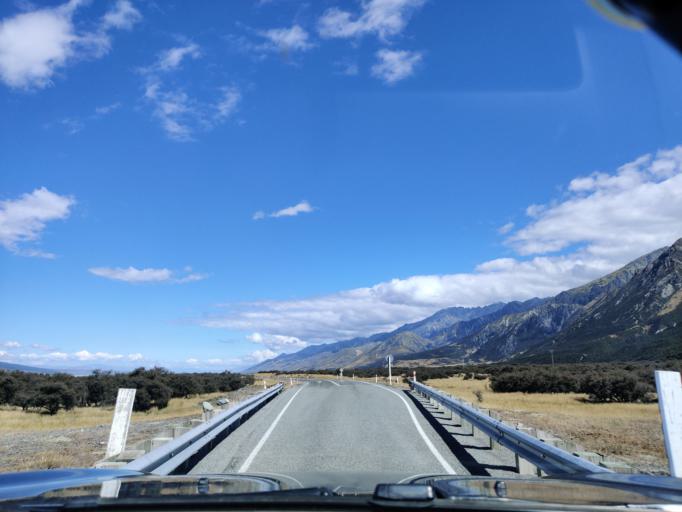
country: NZ
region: Canterbury
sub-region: Timaru District
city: Pleasant Point
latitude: -43.7692
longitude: 170.1229
